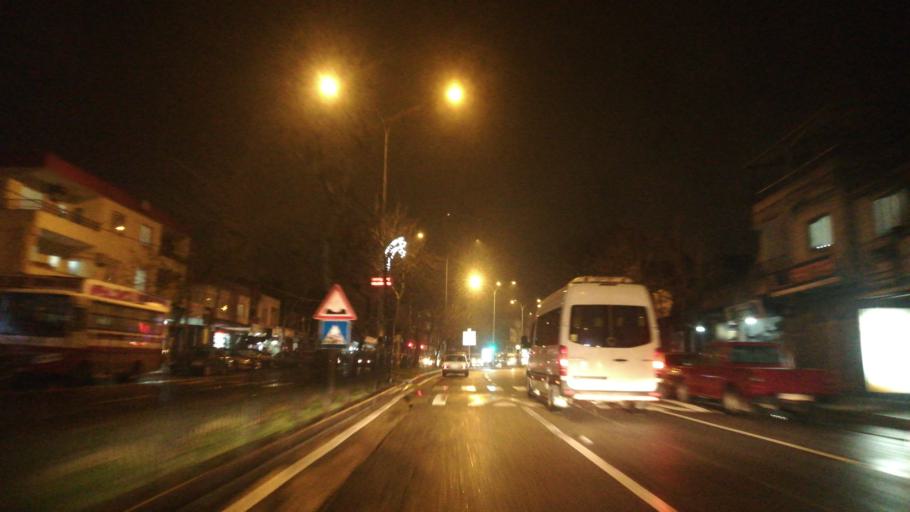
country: TR
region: Kahramanmaras
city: Kahramanmaras
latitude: 37.5732
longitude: 36.8995
